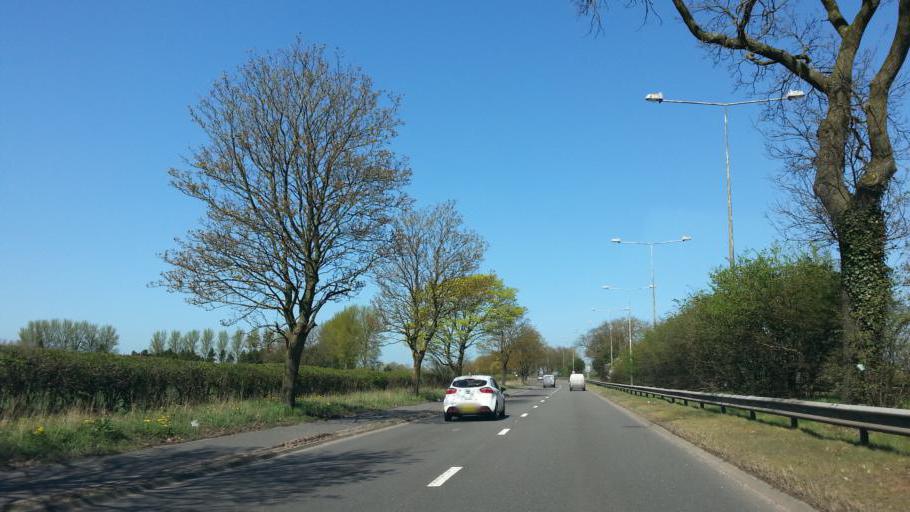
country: GB
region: England
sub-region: Staffordshire
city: Brewood
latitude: 52.6769
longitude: -2.1309
